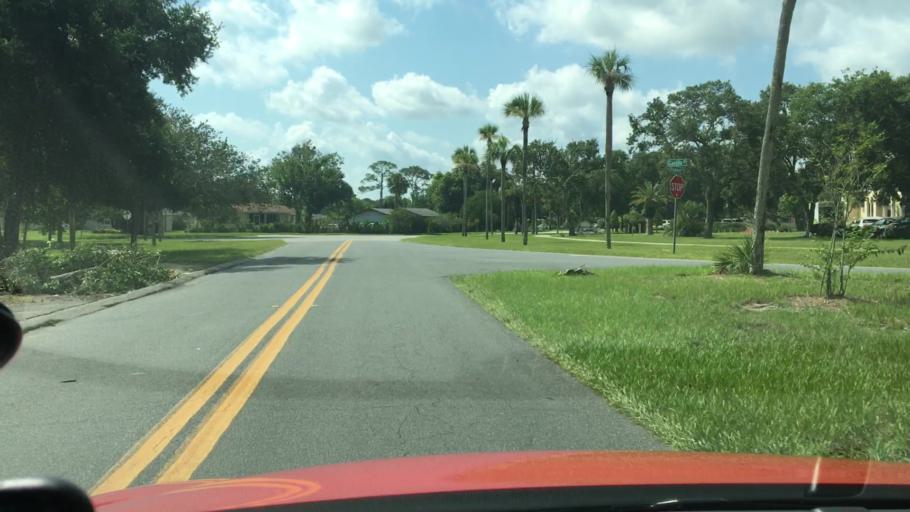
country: US
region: Florida
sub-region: Volusia County
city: Holly Hill
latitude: 29.2628
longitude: -81.0489
